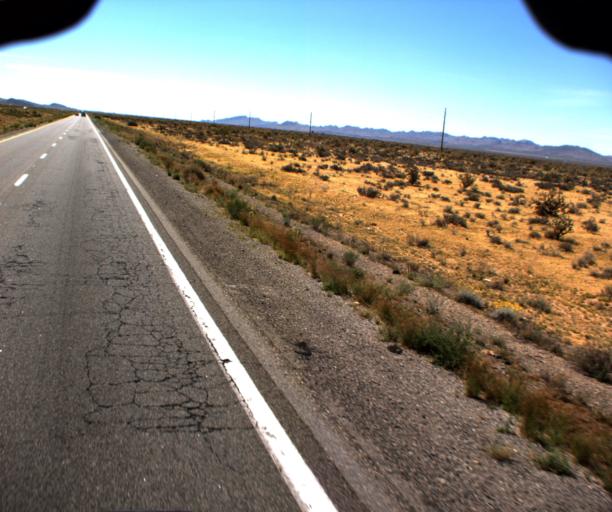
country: US
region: Arizona
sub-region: Mohave County
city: Dolan Springs
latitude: 35.5146
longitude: -114.3423
